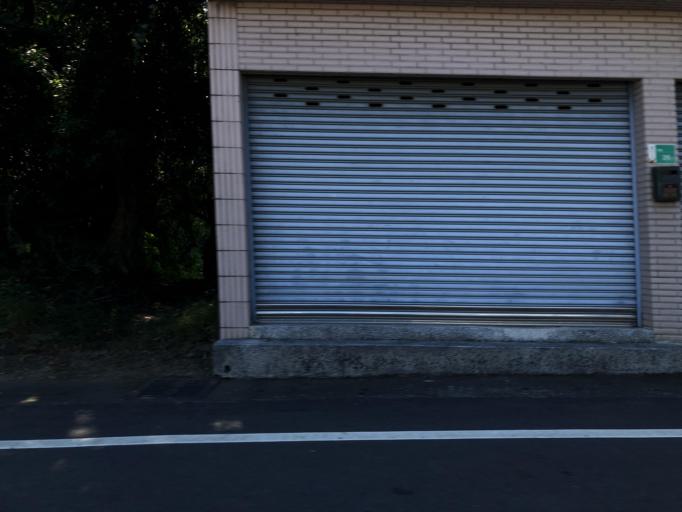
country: TW
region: Taiwan
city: Yujing
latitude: 23.0643
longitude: 120.3861
